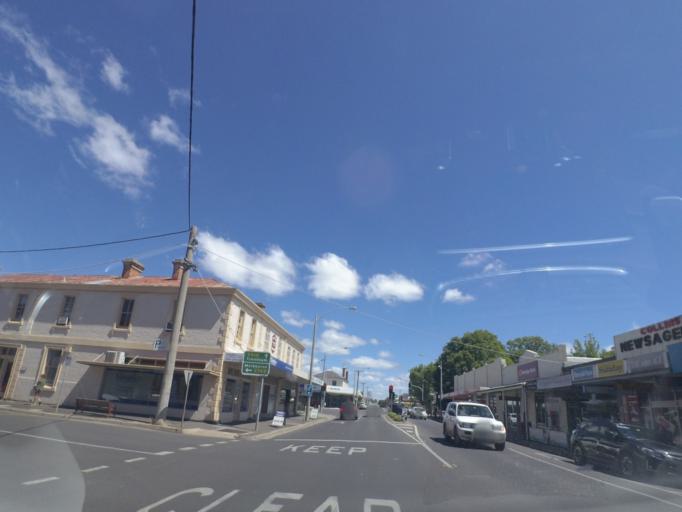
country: AU
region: Victoria
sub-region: Mount Alexander
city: Castlemaine
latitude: -37.2484
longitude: 144.4533
